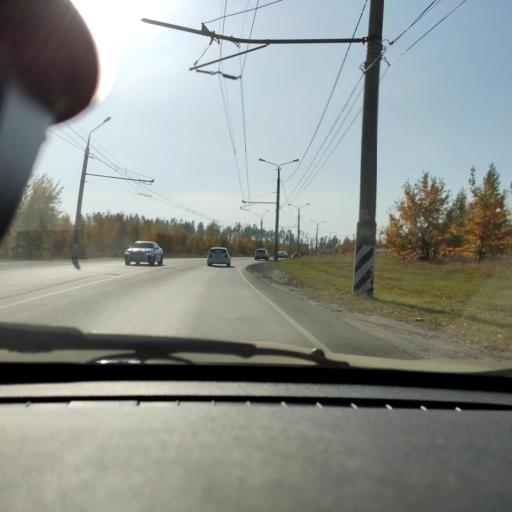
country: RU
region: Samara
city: Tol'yatti
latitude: 53.4833
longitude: 49.3793
